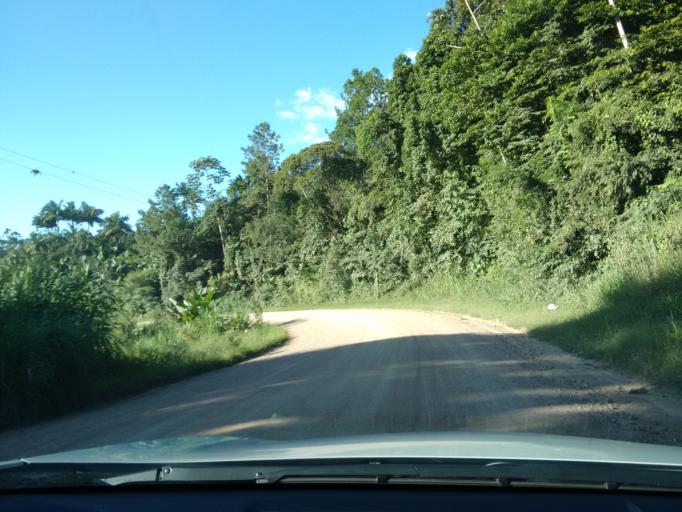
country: BR
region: Santa Catarina
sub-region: Pomerode
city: Pomerode
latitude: -26.7842
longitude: -49.1638
